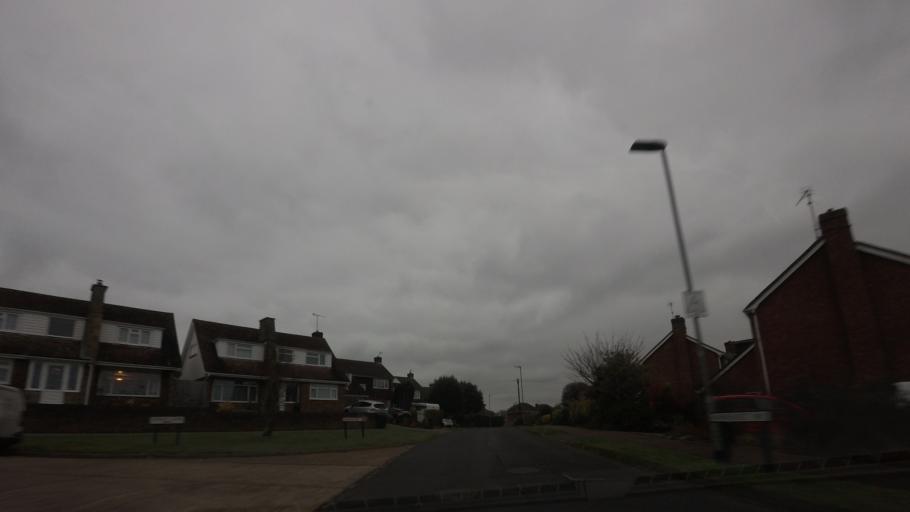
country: GB
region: England
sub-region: East Sussex
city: Bexhill-on-Sea
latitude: 50.8368
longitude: 0.4398
